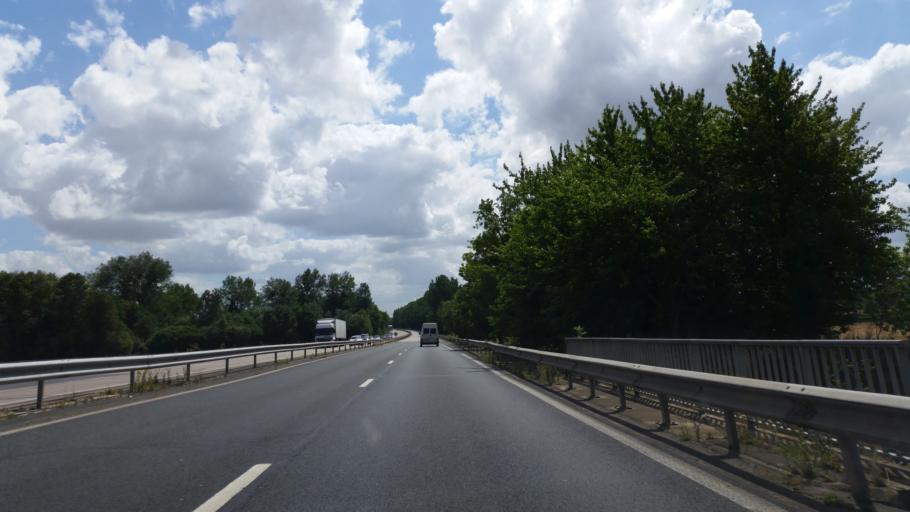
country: FR
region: Lower Normandy
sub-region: Departement du Calvados
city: Potigny
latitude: 48.9581
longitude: -0.2266
